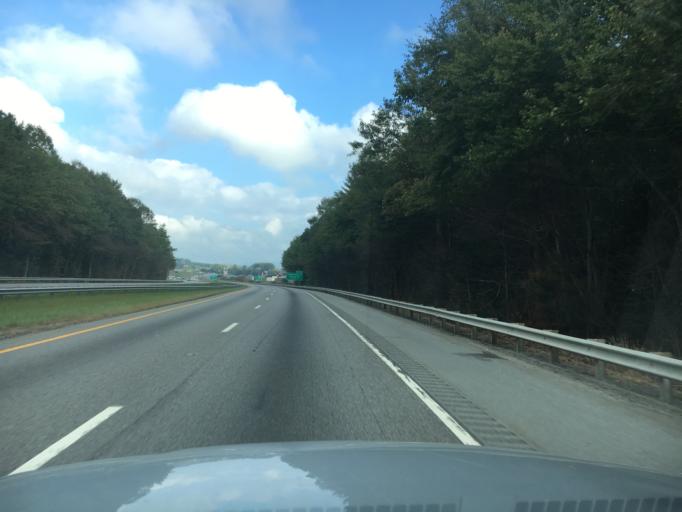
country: US
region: North Carolina
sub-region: Henderson County
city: East Flat Rock
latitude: 35.2899
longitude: -82.4017
